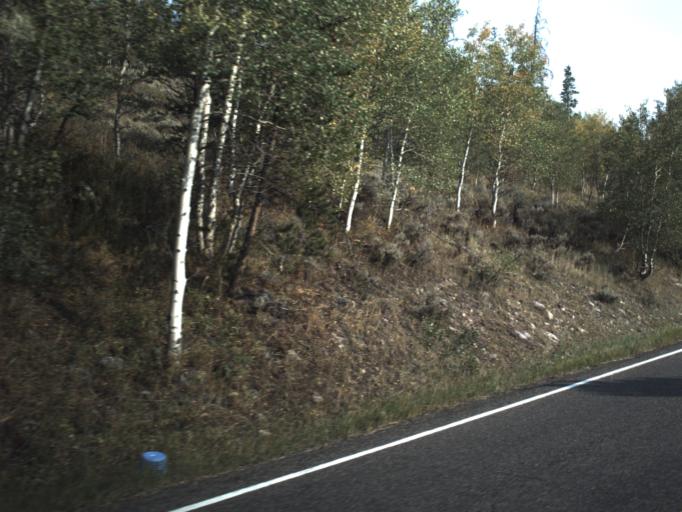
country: US
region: Wyoming
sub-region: Uinta County
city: Evanston
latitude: 40.9075
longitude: -110.8297
